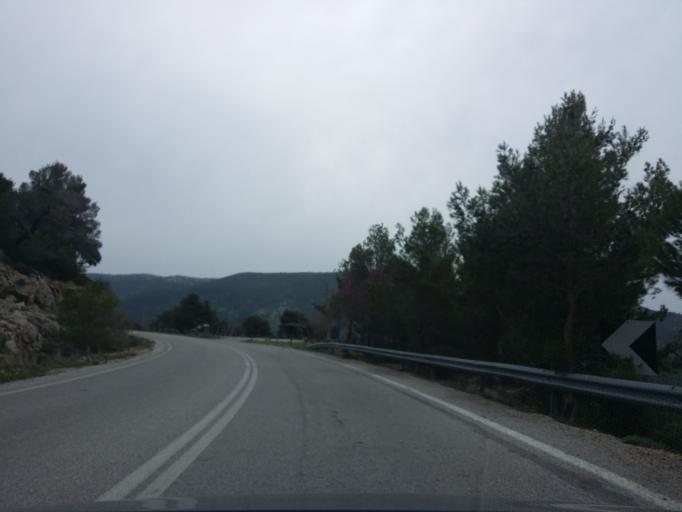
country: GR
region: Central Greece
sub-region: Nomos Voiotias
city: Kaparellion
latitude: 38.1546
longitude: 23.2407
